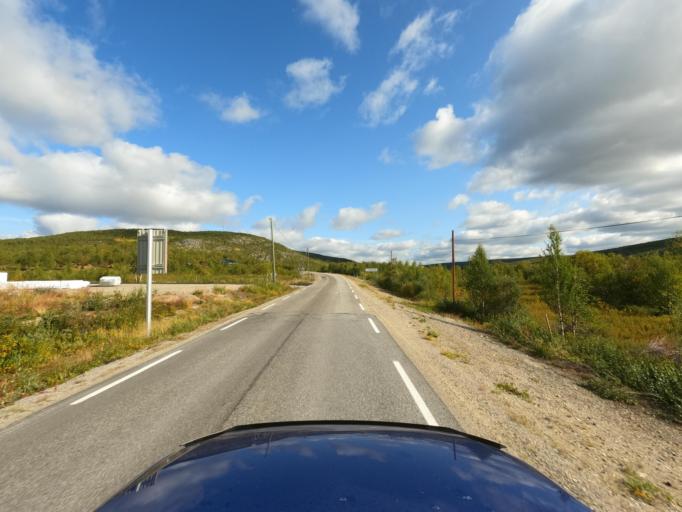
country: NO
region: Finnmark Fylke
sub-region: Porsanger
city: Lakselv
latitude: 69.3999
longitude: 24.6447
